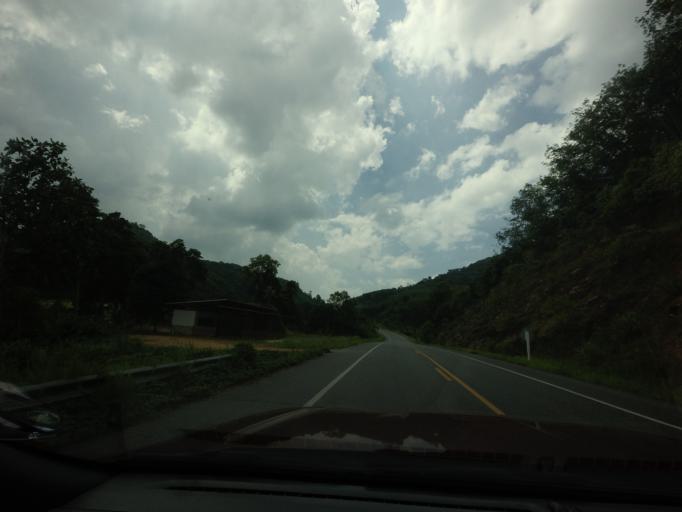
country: TH
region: Yala
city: Than To
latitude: 6.0560
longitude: 101.1935
